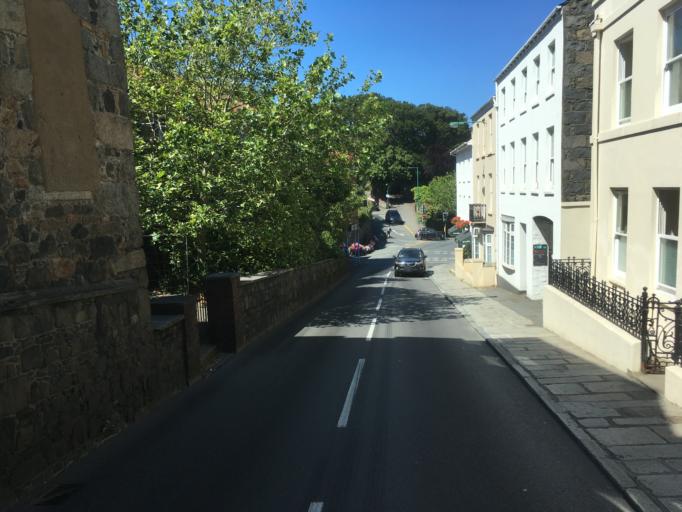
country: GG
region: St Peter Port
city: Saint Peter Port
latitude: 49.4570
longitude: -2.5391
